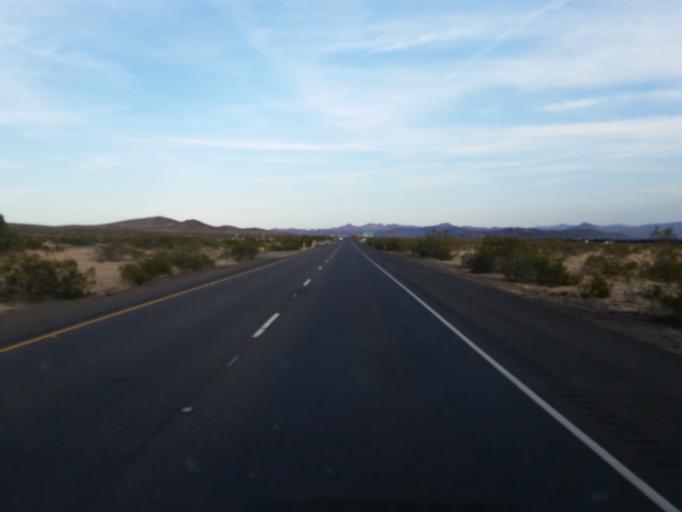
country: US
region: California
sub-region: San Bernardino County
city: Fort Irwin
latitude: 34.7602
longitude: -116.3493
